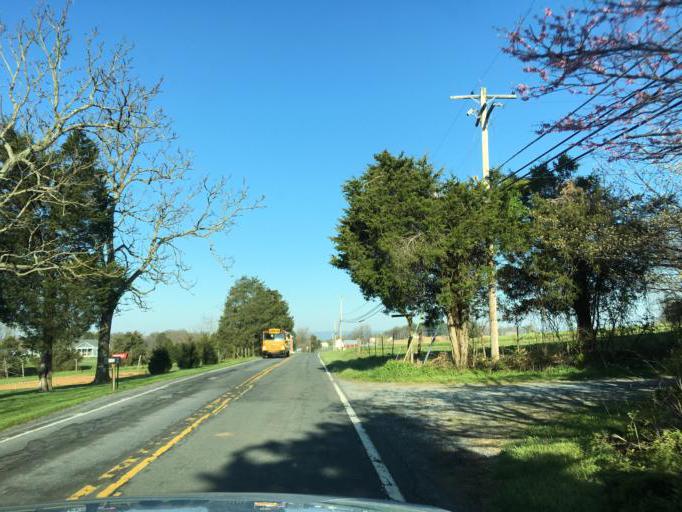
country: US
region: Maryland
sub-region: Frederick County
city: Woodsboro
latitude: 39.4866
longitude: -77.2755
